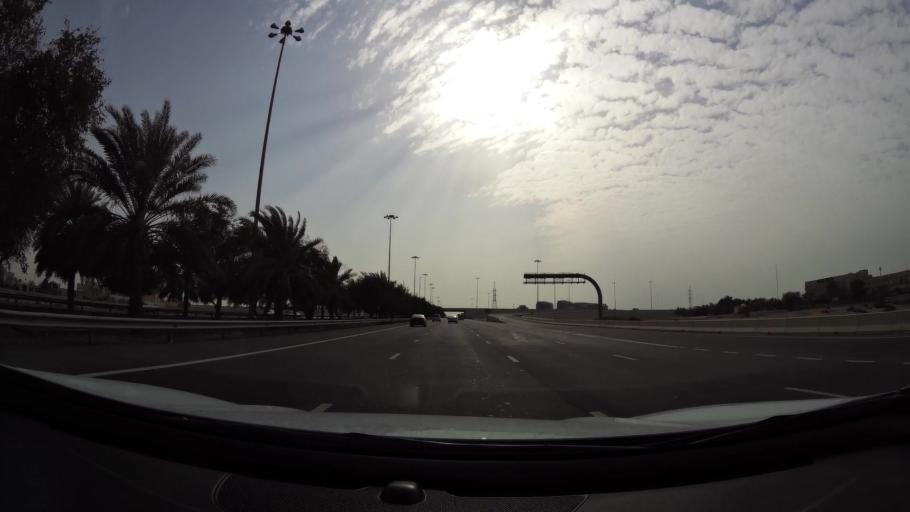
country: AE
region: Abu Dhabi
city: Abu Dhabi
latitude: 24.3294
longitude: 54.6261
